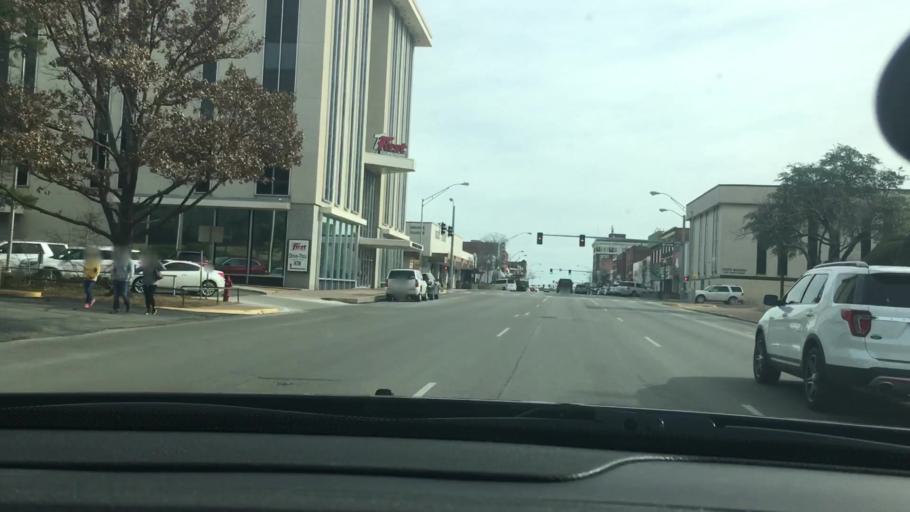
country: US
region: Oklahoma
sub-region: Carter County
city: Ardmore
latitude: 34.1736
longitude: -97.1328
